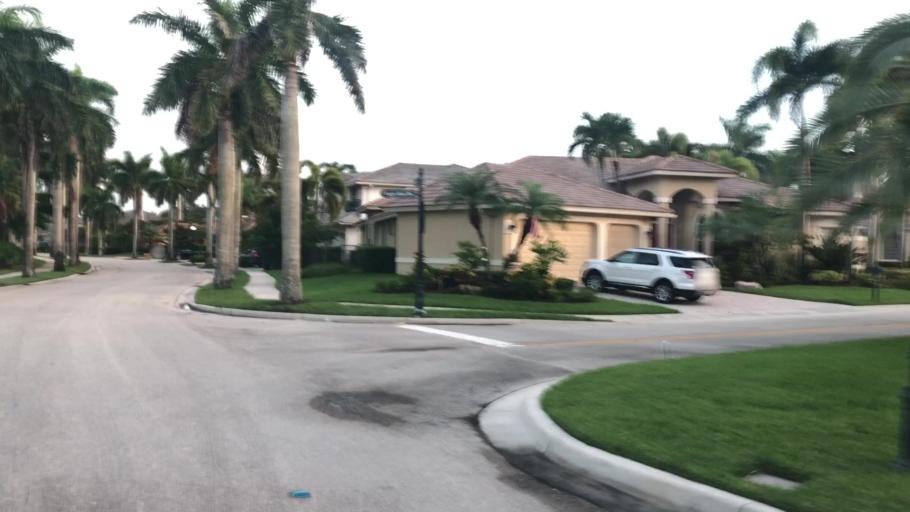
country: US
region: Florida
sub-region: Broward County
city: Weston
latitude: 26.1018
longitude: -80.4002
